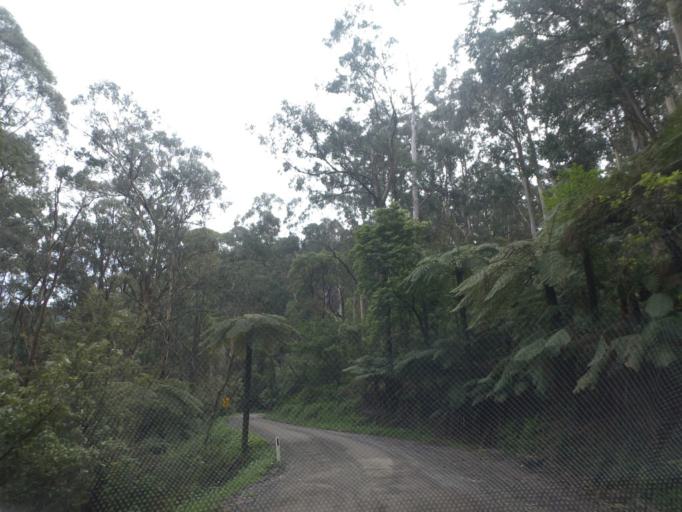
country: AU
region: Victoria
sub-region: Yarra Ranges
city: Kalorama
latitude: -37.8197
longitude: 145.3766
